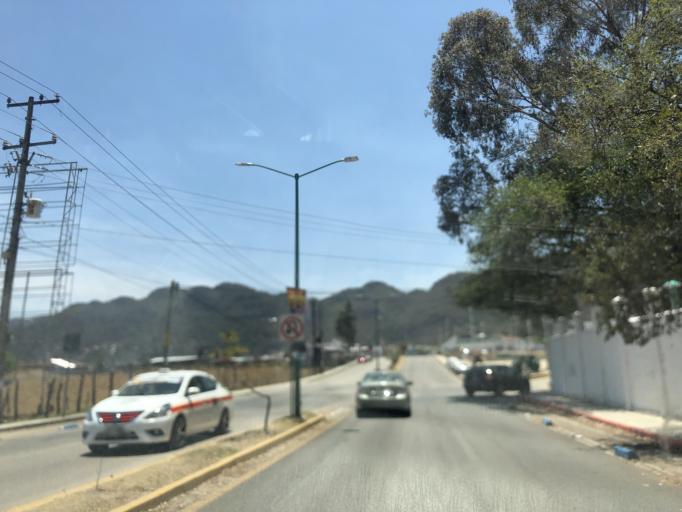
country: MX
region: Chiapas
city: San Cristobal de las Casas
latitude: 16.7246
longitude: -92.6516
